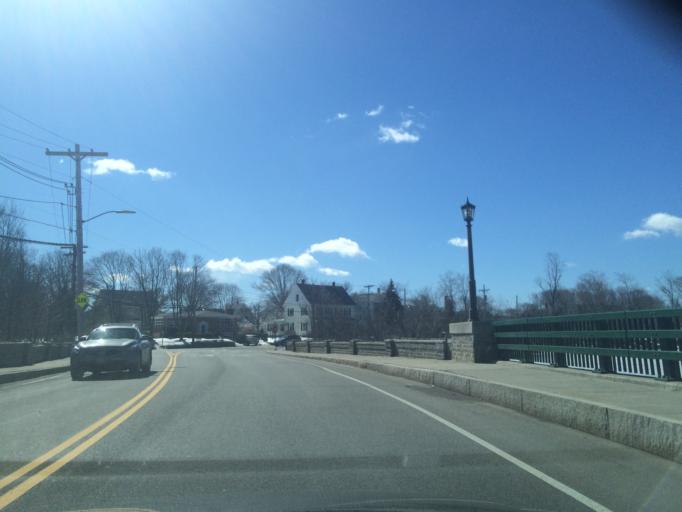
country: US
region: Massachusetts
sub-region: Norfolk County
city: Dedham
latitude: 42.2458
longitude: -71.1364
